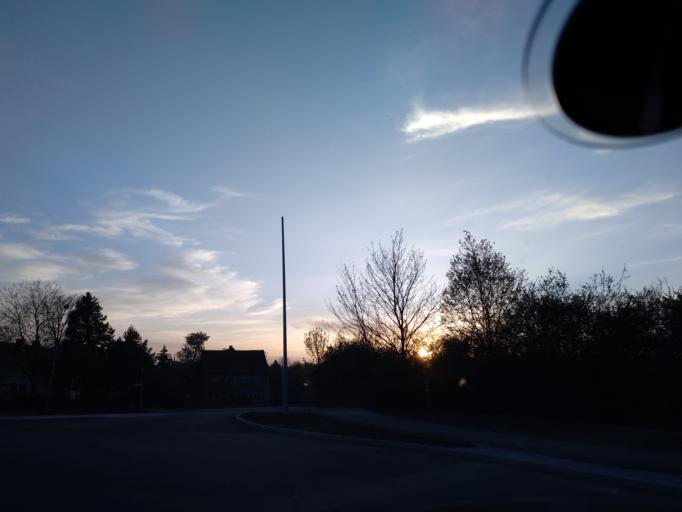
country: DE
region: Baden-Wuerttemberg
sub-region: Regierungsbezirk Stuttgart
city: Satteldorf
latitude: 49.1723
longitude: 10.0877
